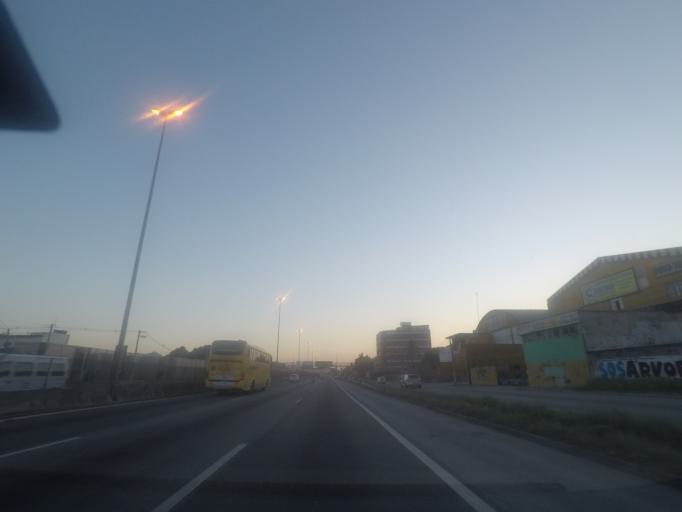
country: BR
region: Rio de Janeiro
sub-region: Duque De Caxias
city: Duque de Caxias
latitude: -22.7925
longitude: -43.2869
